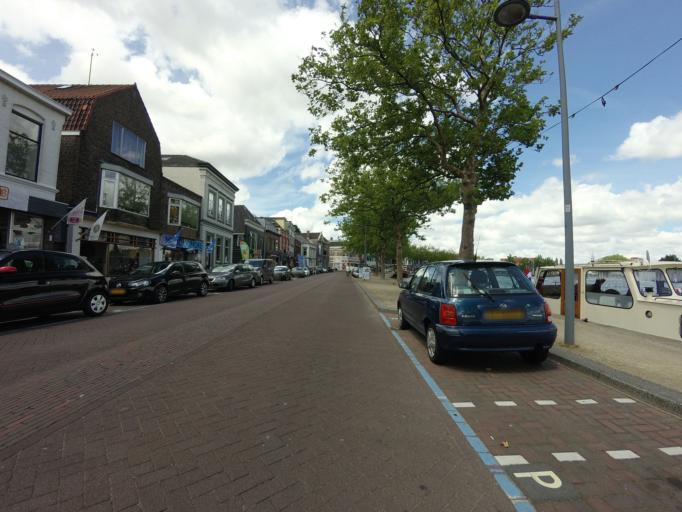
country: NL
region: North Holland
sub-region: Gemeente Zaanstad
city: Zaanstad
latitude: 52.4909
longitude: 4.7919
